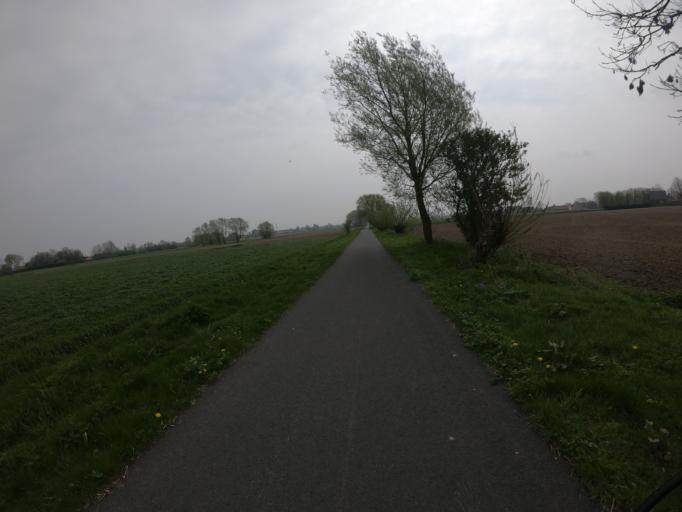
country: BE
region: Flanders
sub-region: Provincie West-Vlaanderen
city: Avelgem
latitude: 50.7756
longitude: 3.4184
